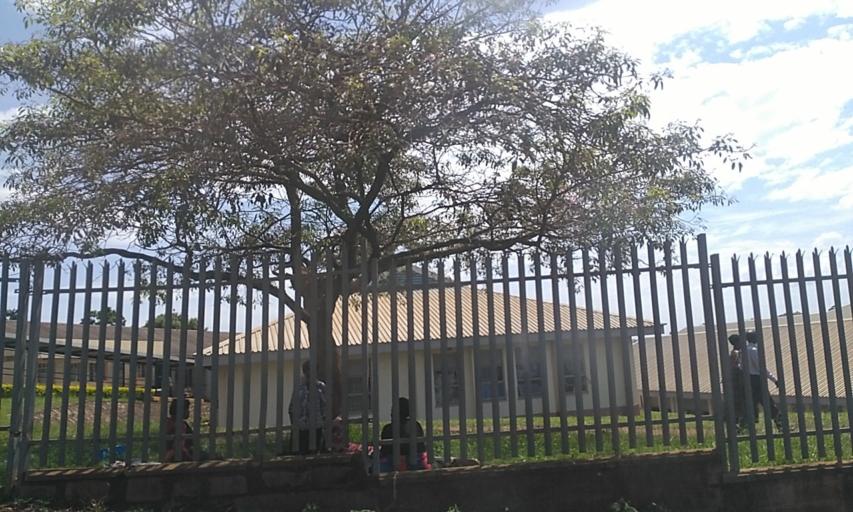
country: UG
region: Central Region
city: Kampala Central Division
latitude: 0.3411
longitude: 32.5762
